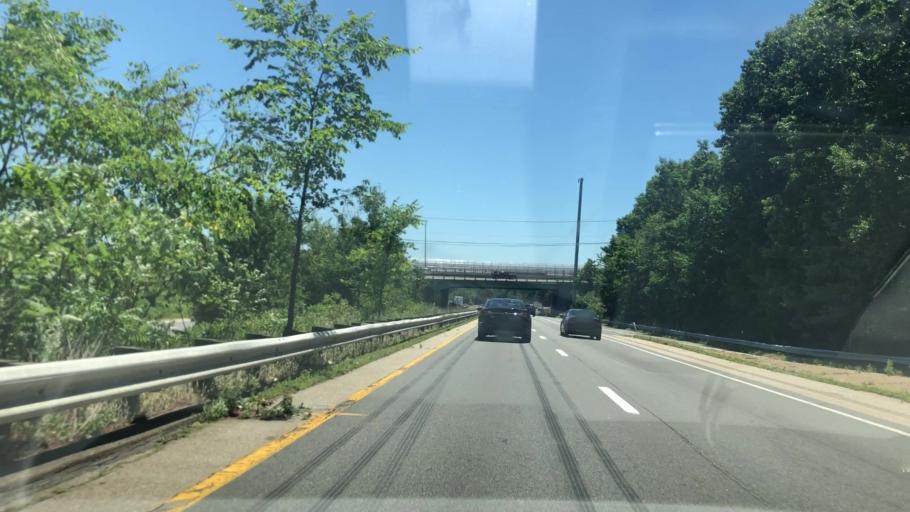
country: US
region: New Hampshire
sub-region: Rockingham County
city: Derry
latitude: 42.8715
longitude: -71.3416
